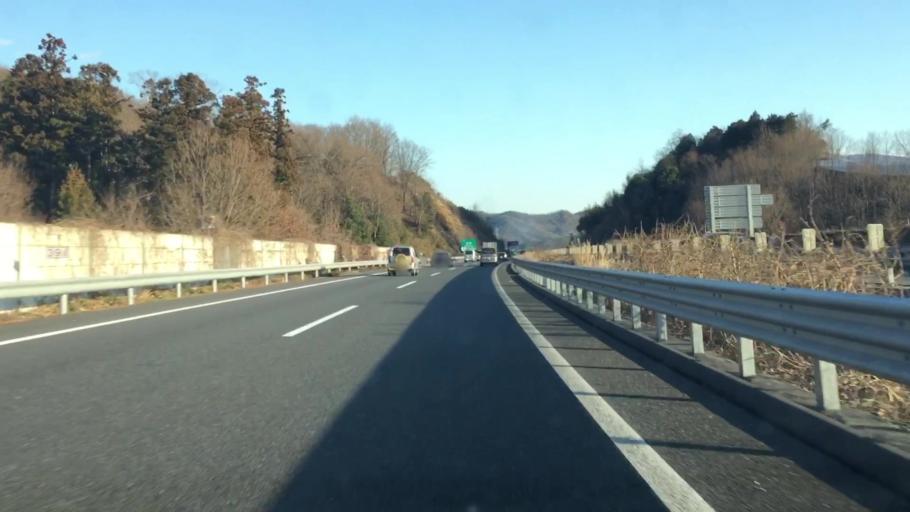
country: JP
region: Tochigi
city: Ashikaga
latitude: 36.3665
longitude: 139.4734
